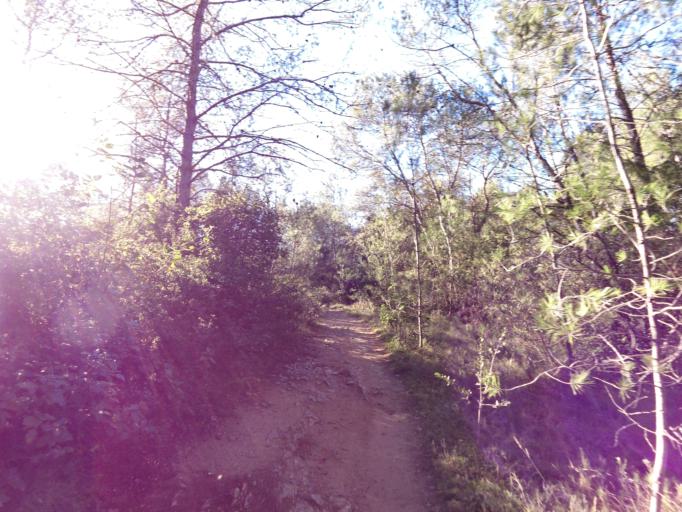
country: FR
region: Languedoc-Roussillon
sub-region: Departement du Gard
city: Aubais
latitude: 43.7387
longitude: 4.1566
